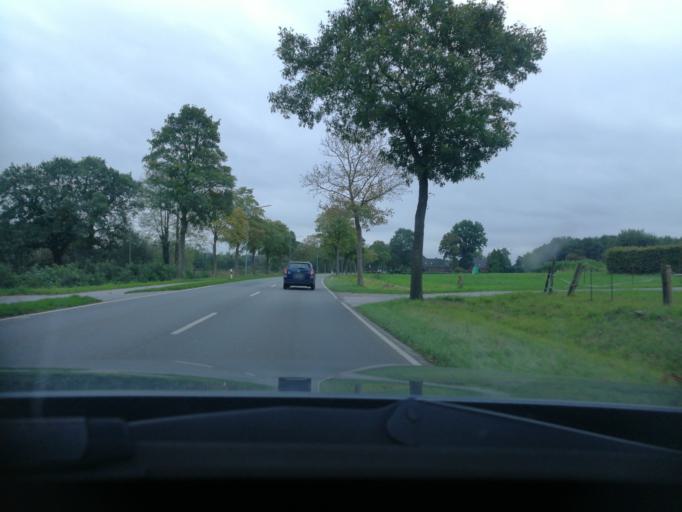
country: DE
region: North Rhine-Westphalia
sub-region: Regierungsbezirk Dusseldorf
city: Kevelaer
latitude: 51.5314
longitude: 6.2424
